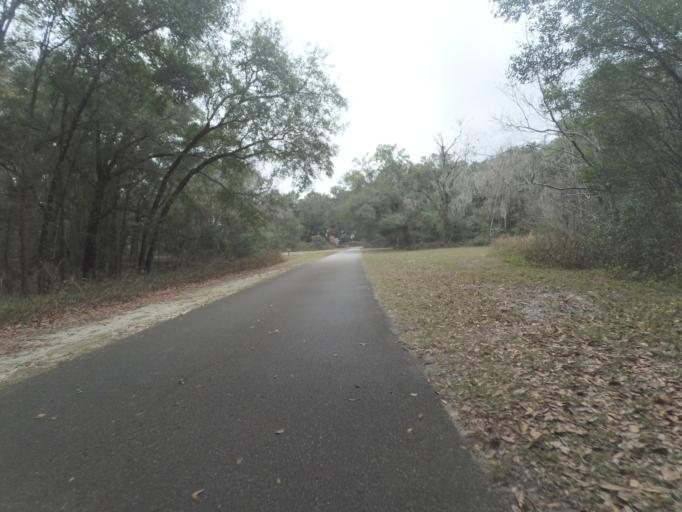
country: US
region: Florida
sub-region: Alachua County
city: Gainesville
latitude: 29.6103
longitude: -82.3034
